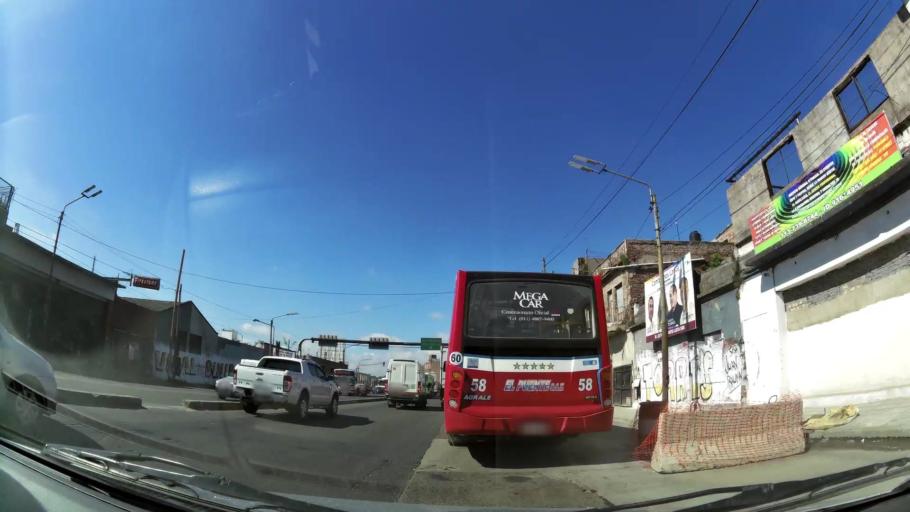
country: AR
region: Buenos Aires
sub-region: Partido de Lanus
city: Lanus
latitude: -34.6642
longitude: -58.4177
